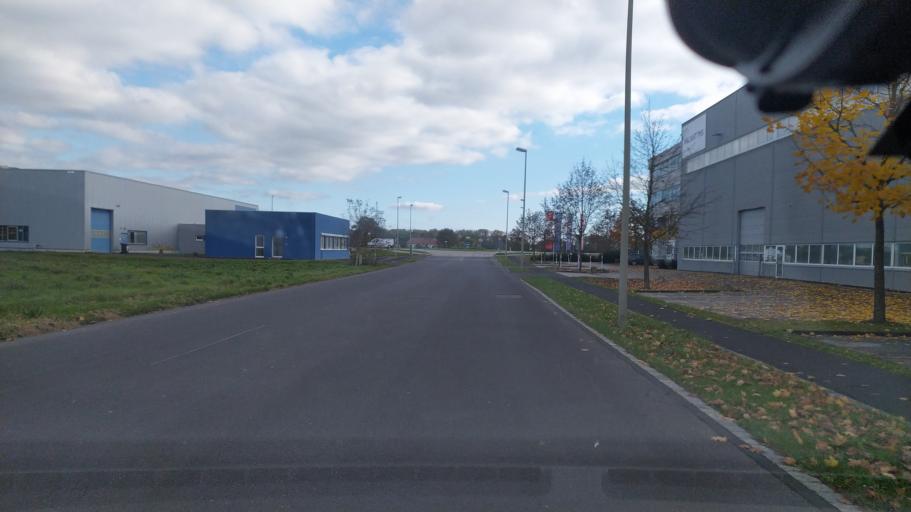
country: AT
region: Upper Austria
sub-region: Politischer Bezirk Urfahr-Umgebung
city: Steyregg
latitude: 48.2495
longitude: 14.3812
